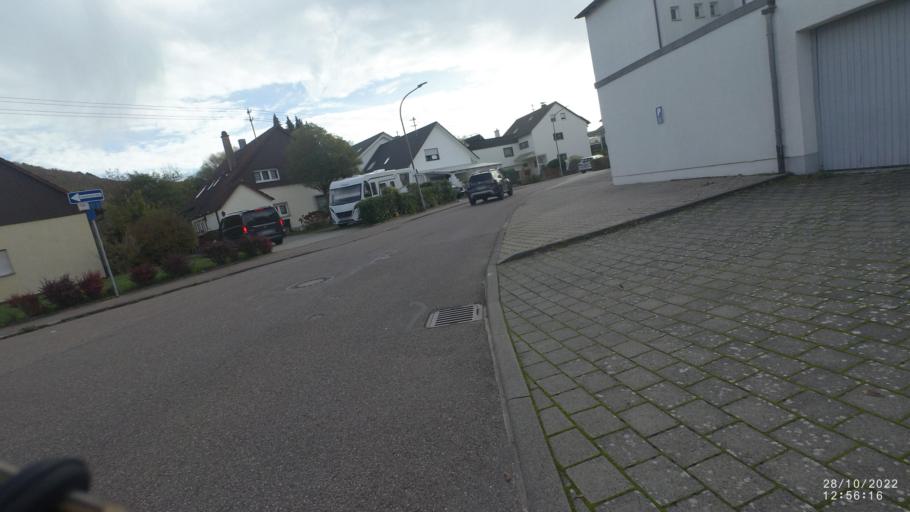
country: DE
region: Baden-Wuerttemberg
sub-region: Regierungsbezirk Stuttgart
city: Kuchen
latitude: 48.6415
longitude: 9.7962
